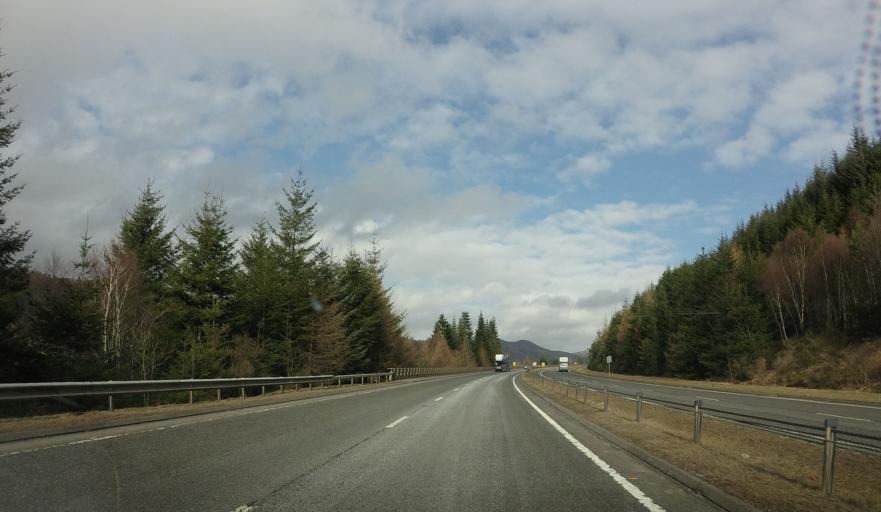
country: GB
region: Scotland
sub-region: Perth and Kinross
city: Pitlochry
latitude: 56.7278
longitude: -3.7737
